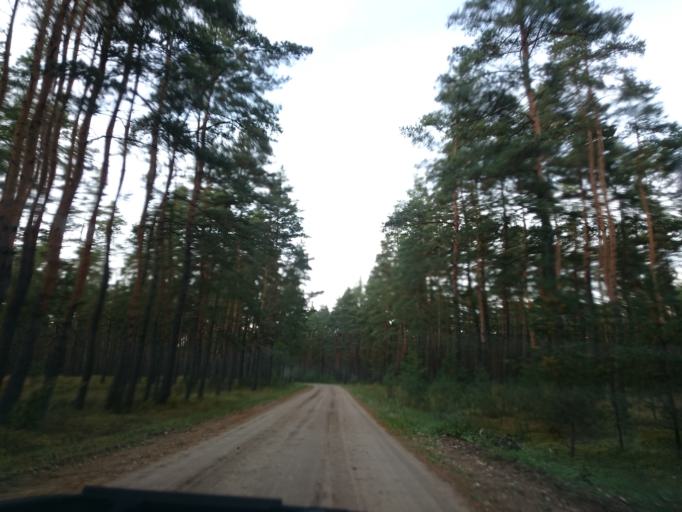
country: LV
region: Garkalne
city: Garkalne
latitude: 57.0423
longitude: 24.3872
